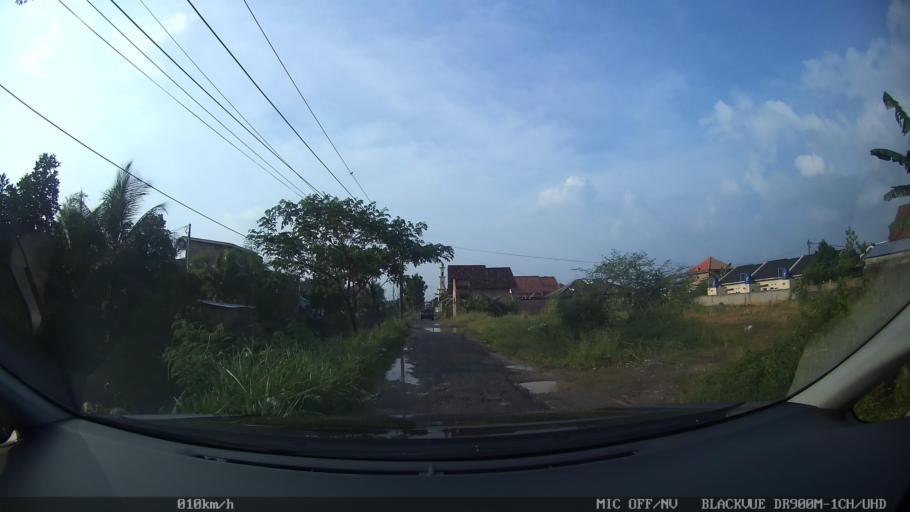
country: ID
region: Lampung
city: Kedaton
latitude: -5.3932
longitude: 105.3087
